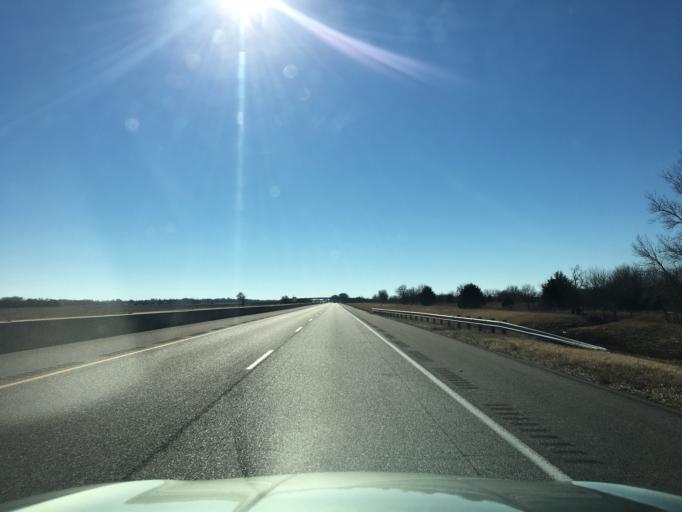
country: US
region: Kansas
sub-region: Sumner County
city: Belle Plaine
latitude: 37.4574
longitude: -97.3225
